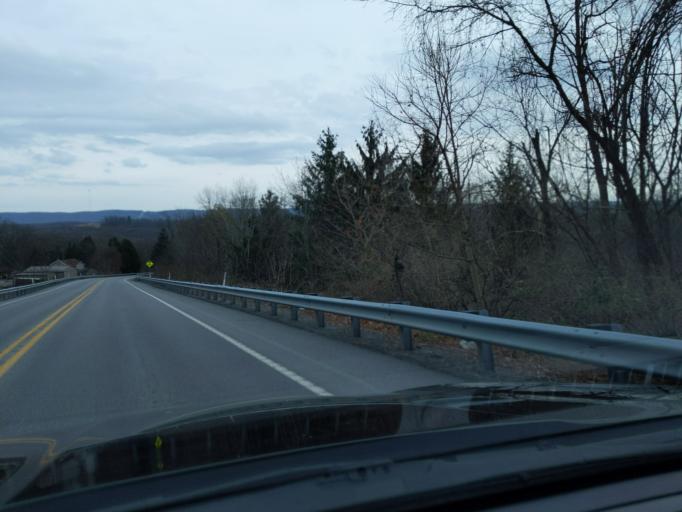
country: US
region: Pennsylvania
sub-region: Blair County
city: Lakemont
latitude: 40.4605
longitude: -78.3619
